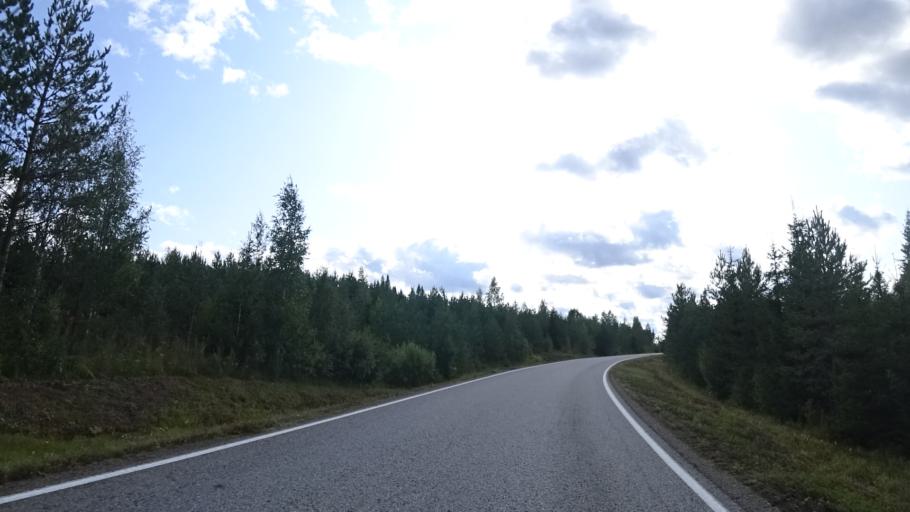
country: RU
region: Republic of Karelia
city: Vyartsilya
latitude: 62.2662
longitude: 30.7806
